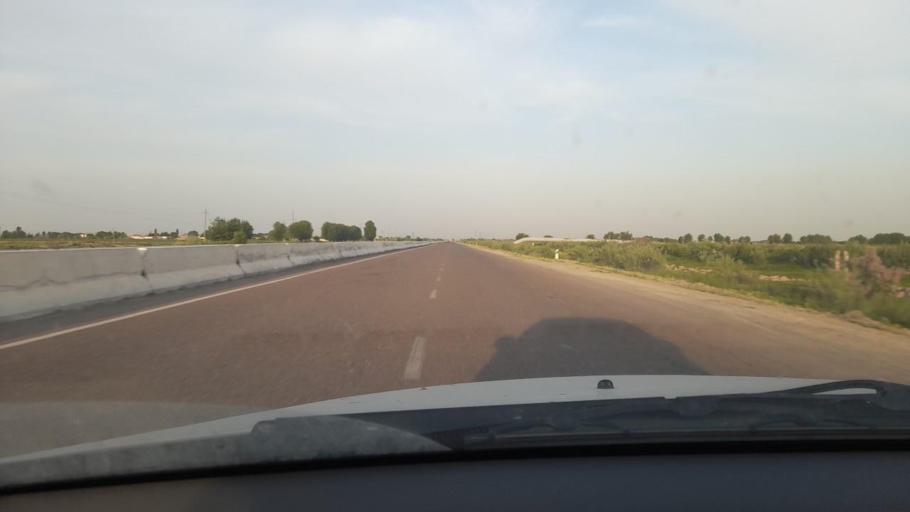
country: UZ
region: Sirdaryo
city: Guliston
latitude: 40.4938
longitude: 68.6628
